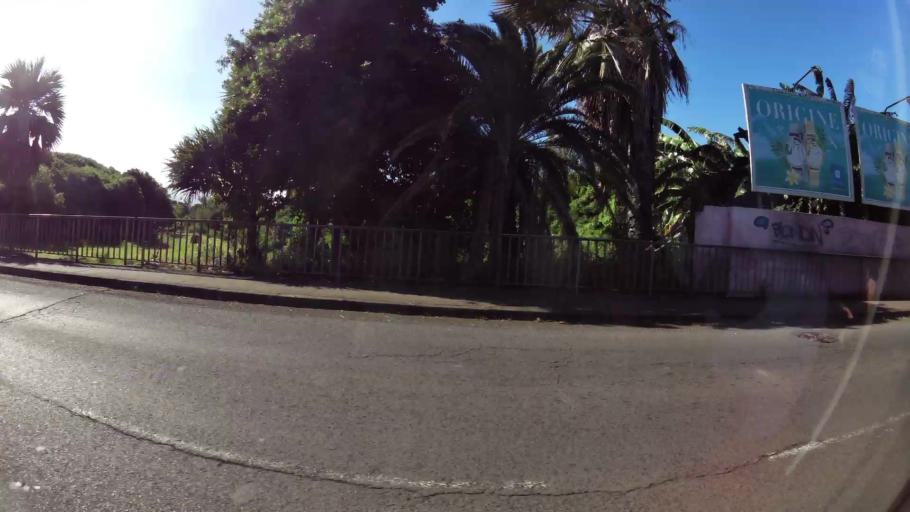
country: RE
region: Reunion
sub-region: Reunion
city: Saint-Pierre
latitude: -21.3460
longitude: 55.4883
